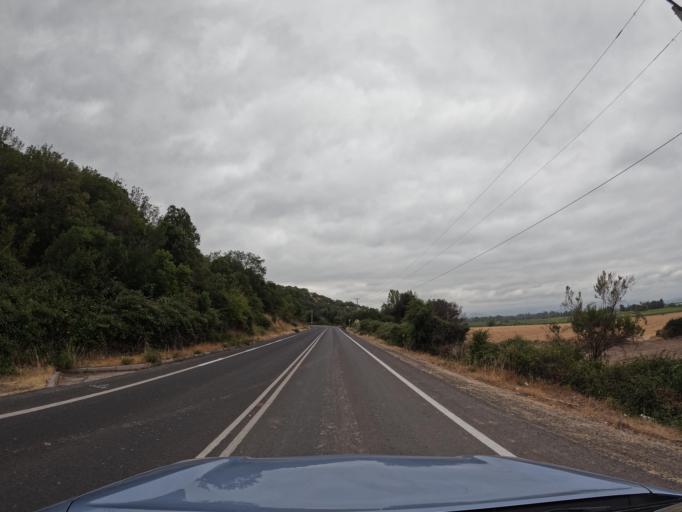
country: CL
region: O'Higgins
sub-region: Provincia de Colchagua
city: Chimbarongo
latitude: -34.7281
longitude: -71.1028
